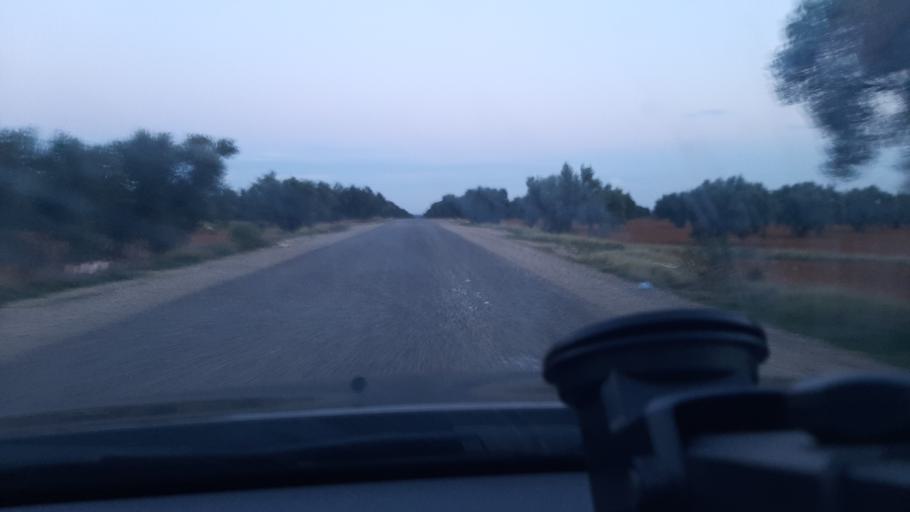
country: TN
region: Al Mahdiyah
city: Shurban
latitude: 35.0315
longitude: 10.4973
